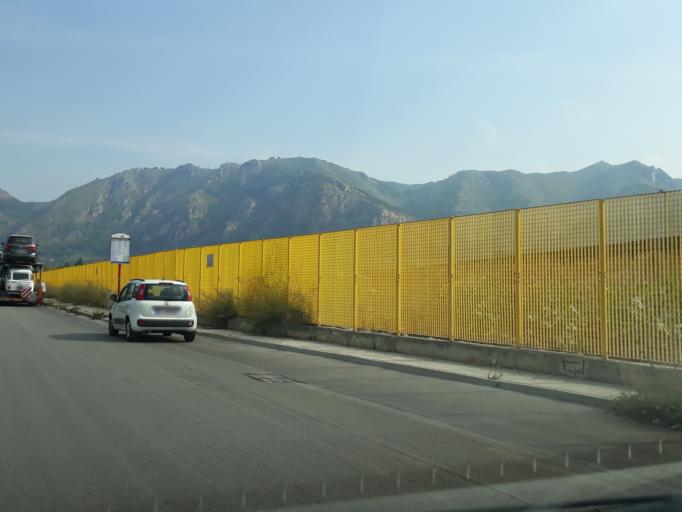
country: IT
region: Sicily
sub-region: Palermo
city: Villa Ciambra
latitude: 38.0919
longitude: 13.3414
